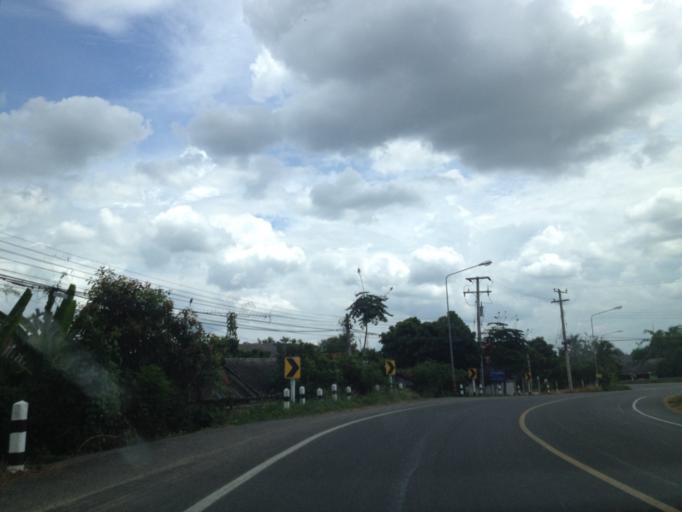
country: TH
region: Chiang Mai
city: San Pa Tong
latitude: 18.6355
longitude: 98.8495
